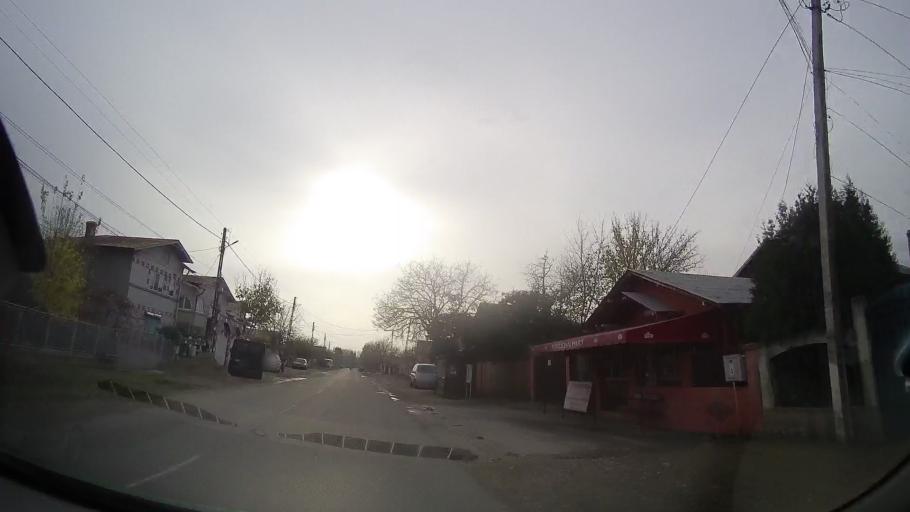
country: RO
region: Prahova
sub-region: Comuna Balta Doamnei
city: Balta Doamnei
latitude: 44.7638
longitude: 26.1442
